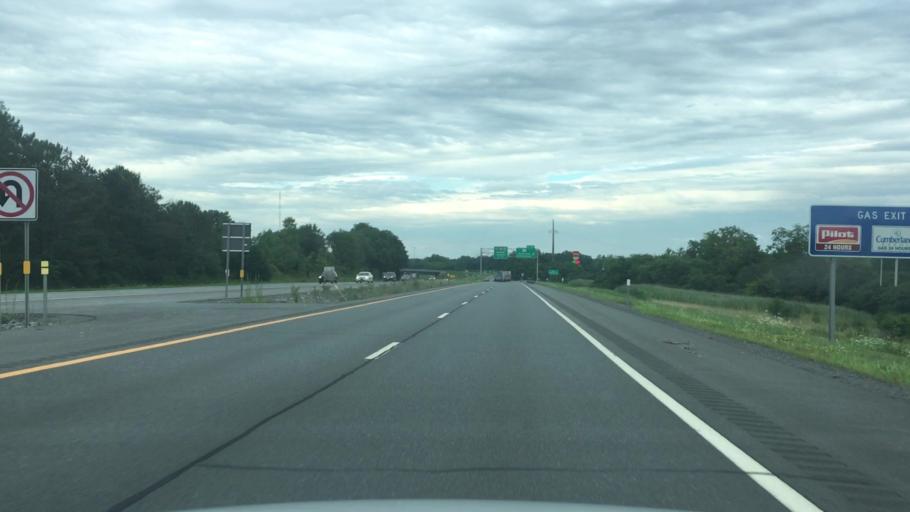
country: US
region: New York
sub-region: Schenectady County
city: Rotterdam
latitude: 42.7813
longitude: -74.0358
